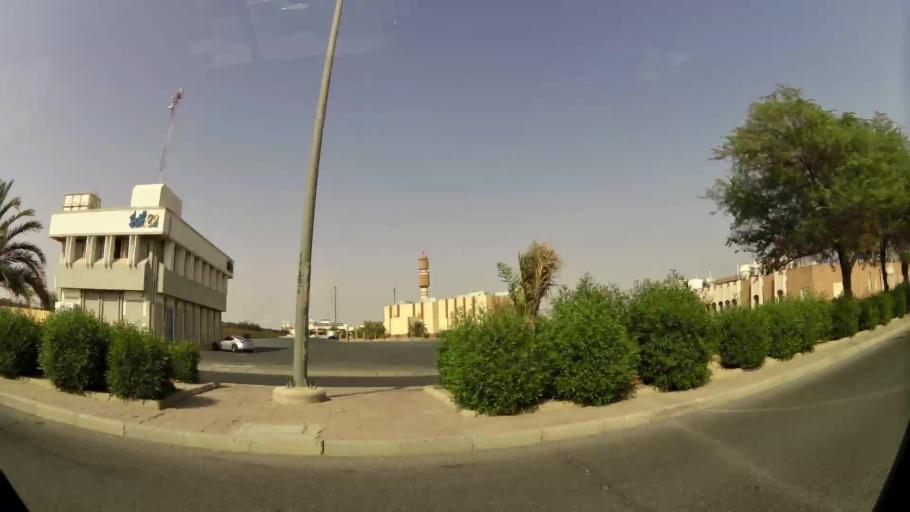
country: KW
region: Muhafazat al Jahra'
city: Al Jahra'
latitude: 29.3420
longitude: 47.6582
